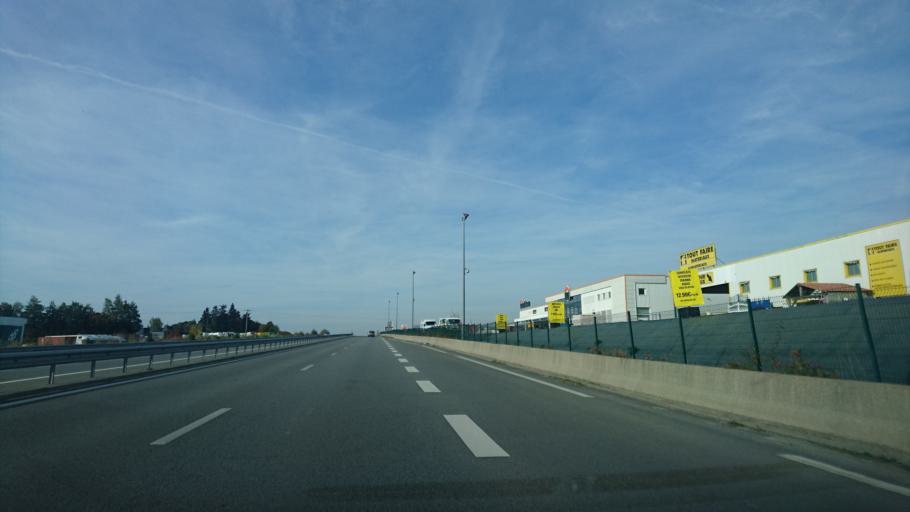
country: FR
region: Brittany
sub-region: Departement d'Ille-et-Vilaine
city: Corps-Nuds
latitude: 47.9727
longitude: -1.5407
